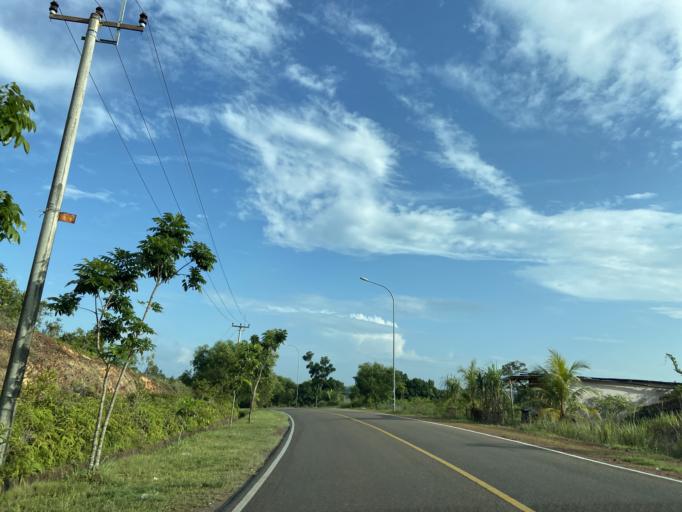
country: ID
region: Riau Islands
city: Tanjungpinang
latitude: 0.9494
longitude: 104.0554
